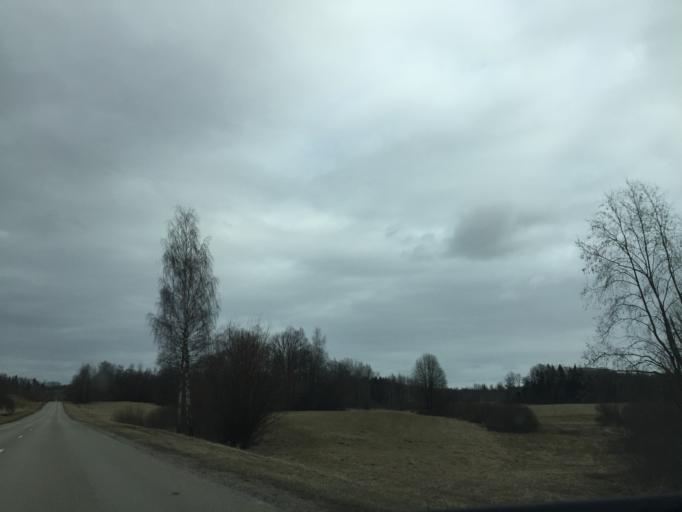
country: LV
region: Kraslavas Rajons
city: Kraslava
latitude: 55.9635
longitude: 27.1674
